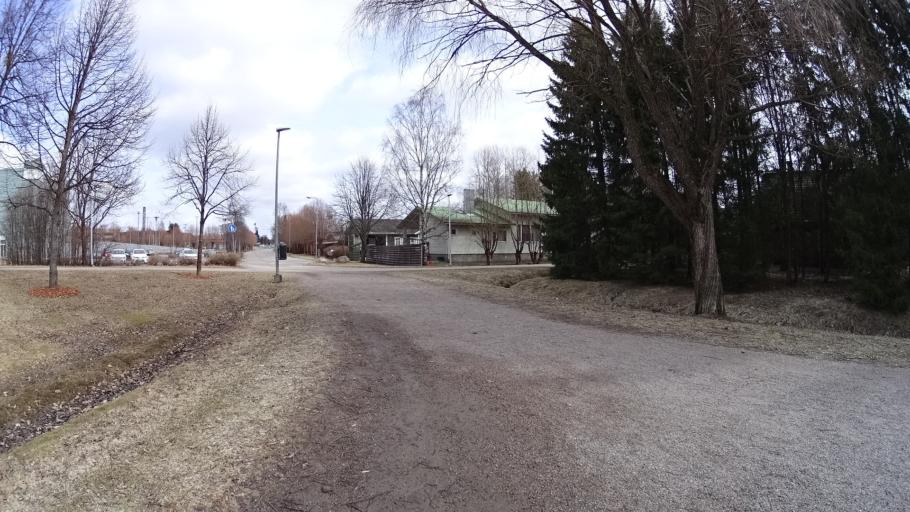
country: FI
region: Uusimaa
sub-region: Helsinki
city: Kilo
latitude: 60.2688
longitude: 24.8008
